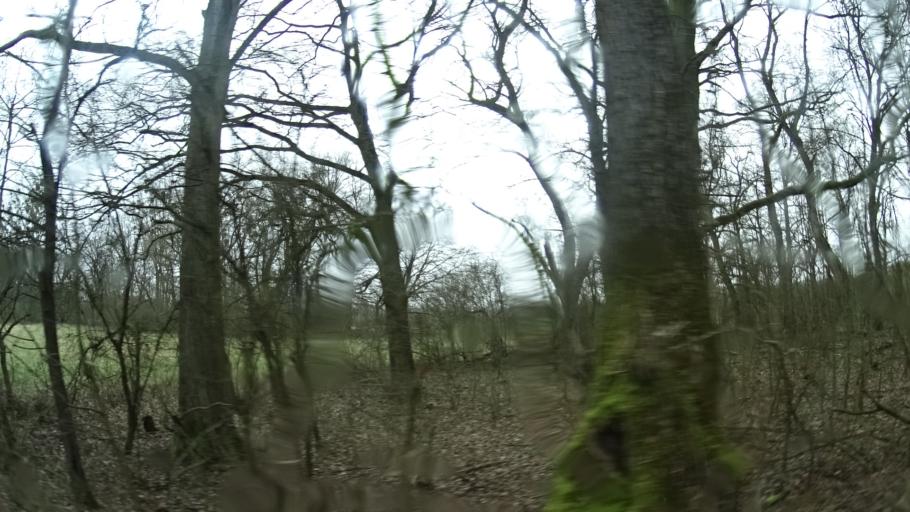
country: DE
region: Hesse
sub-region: Regierungsbezirk Darmstadt
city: Stockstadt am Rhein
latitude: 49.8313
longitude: 8.4193
